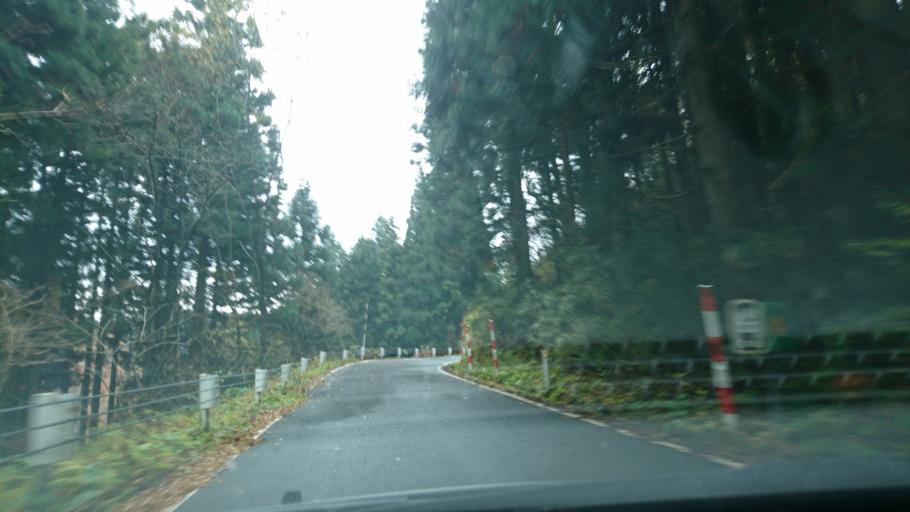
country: JP
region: Iwate
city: Ichinoseki
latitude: 38.9095
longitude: 140.9068
